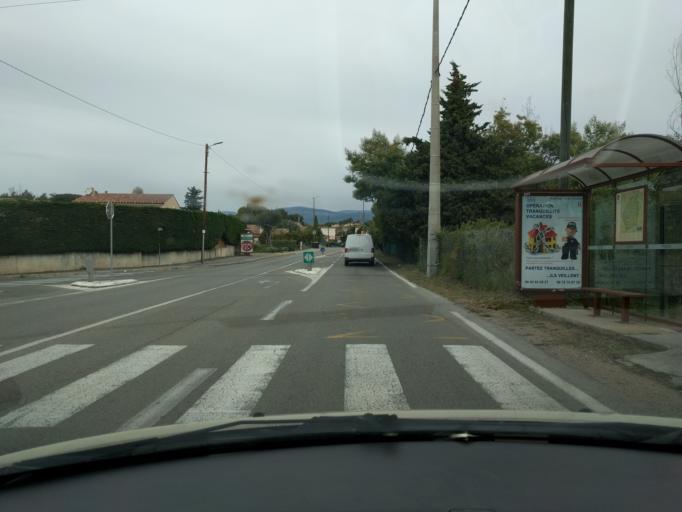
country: FR
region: Provence-Alpes-Cote d'Azur
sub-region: Departement des Alpes-Maritimes
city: La Roquette-sur-Siagne
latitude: 43.5948
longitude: 6.9566
